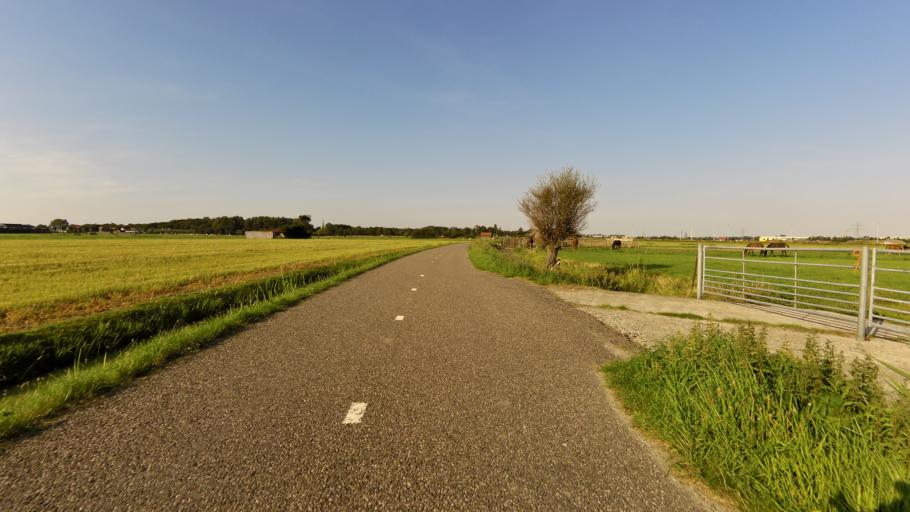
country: NL
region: South Holland
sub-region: Gemeente Teylingen
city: Voorhout
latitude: 52.2089
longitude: 4.4763
